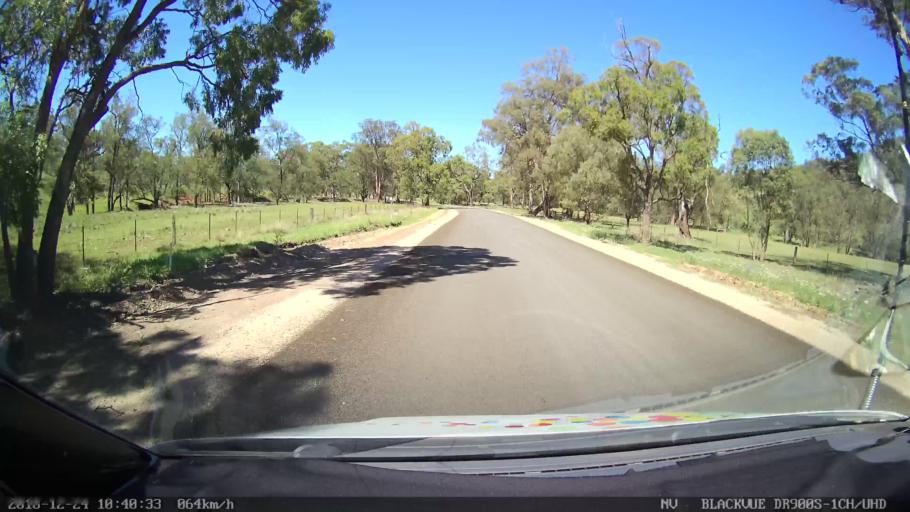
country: AU
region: New South Wales
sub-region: Upper Hunter Shire
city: Merriwa
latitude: -31.8623
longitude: 150.4664
